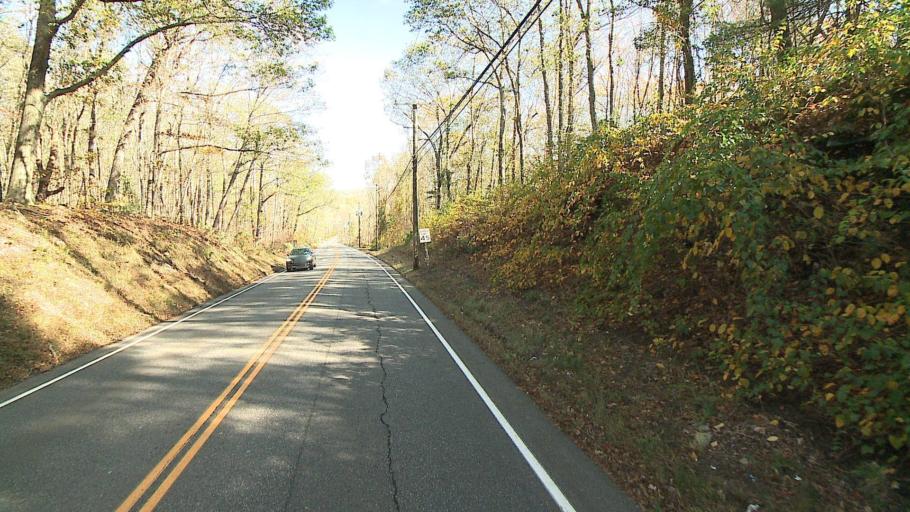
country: US
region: Connecticut
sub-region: Tolland County
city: Storrs
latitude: 41.8581
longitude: -72.1739
